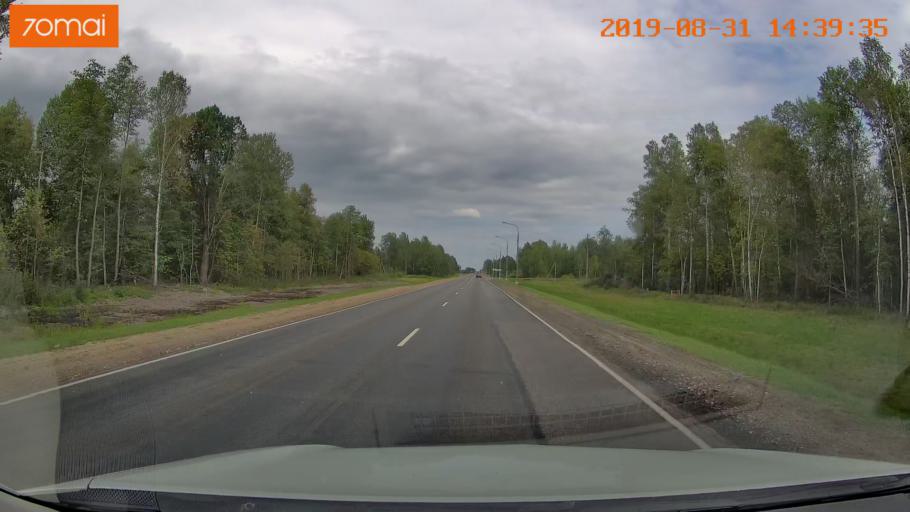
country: RU
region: Smolensk
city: Yekimovichi
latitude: 54.1926
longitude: 33.5561
